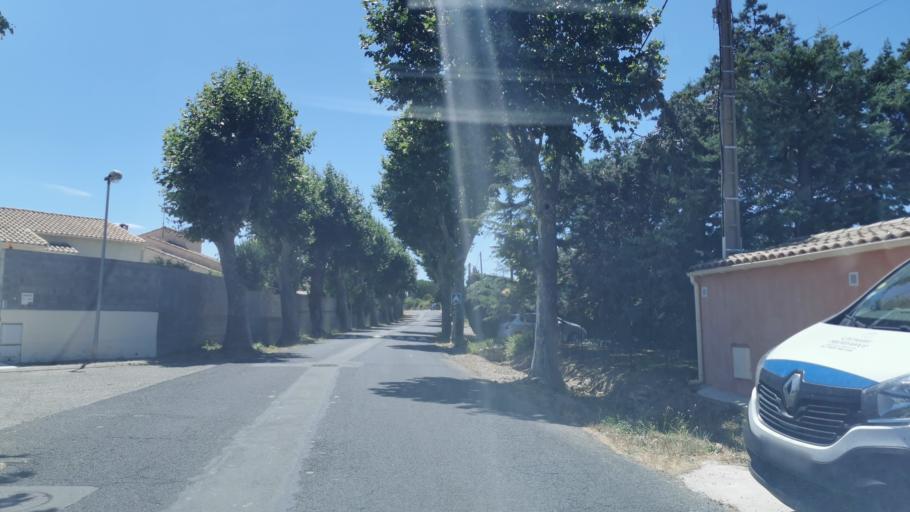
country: FR
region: Languedoc-Roussillon
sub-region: Departement de l'Herault
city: Nissan-lez-Enserune
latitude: 43.2864
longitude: 3.1260
